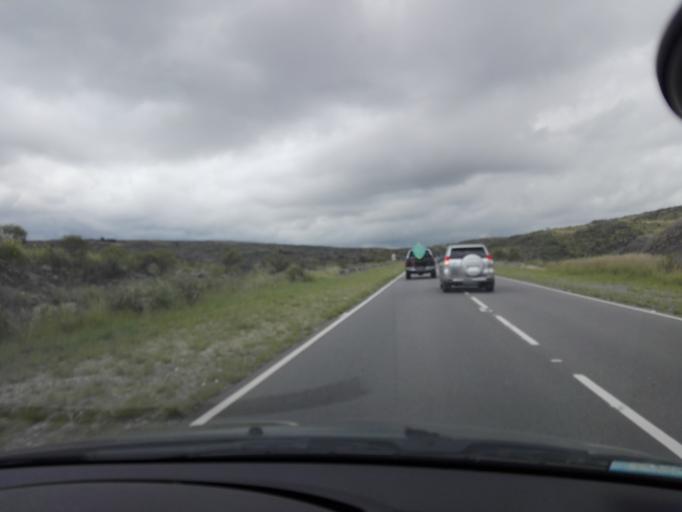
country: AR
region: Cordoba
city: Cuesta Blanca
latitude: -31.5741
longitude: -64.6445
